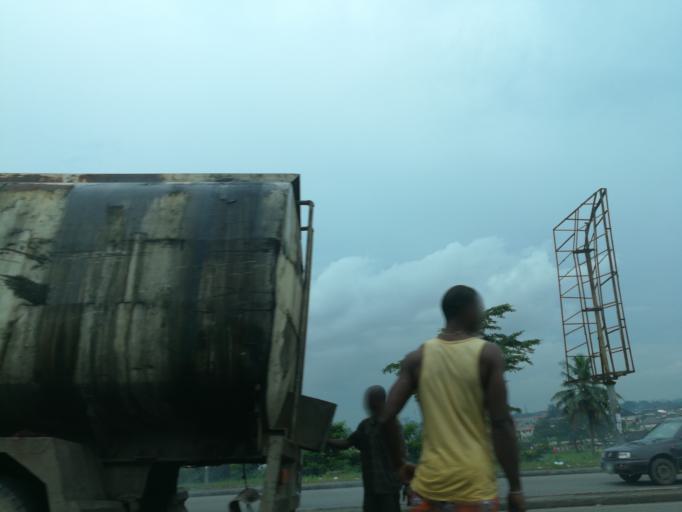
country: NG
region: Rivers
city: Port Harcourt
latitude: 4.8082
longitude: 7.0100
